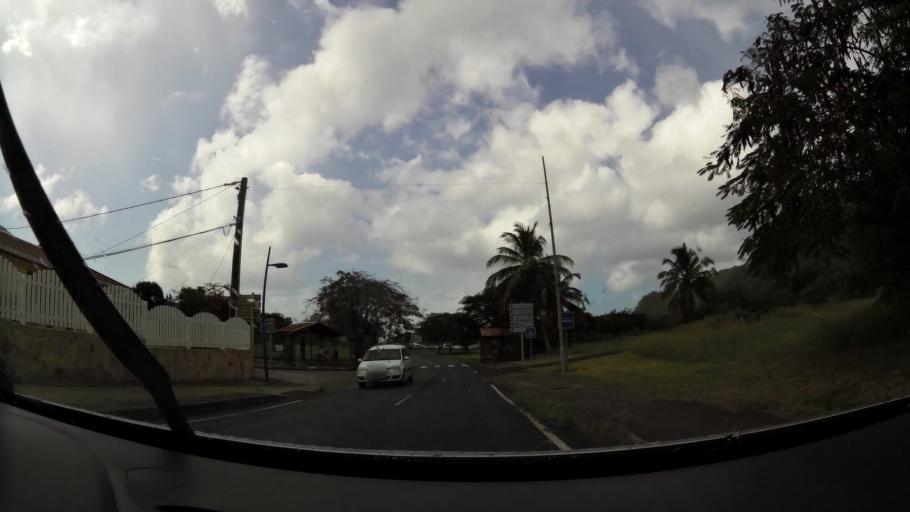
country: MQ
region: Martinique
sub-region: Martinique
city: Les Trois-Ilets
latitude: 14.4932
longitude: -61.0784
